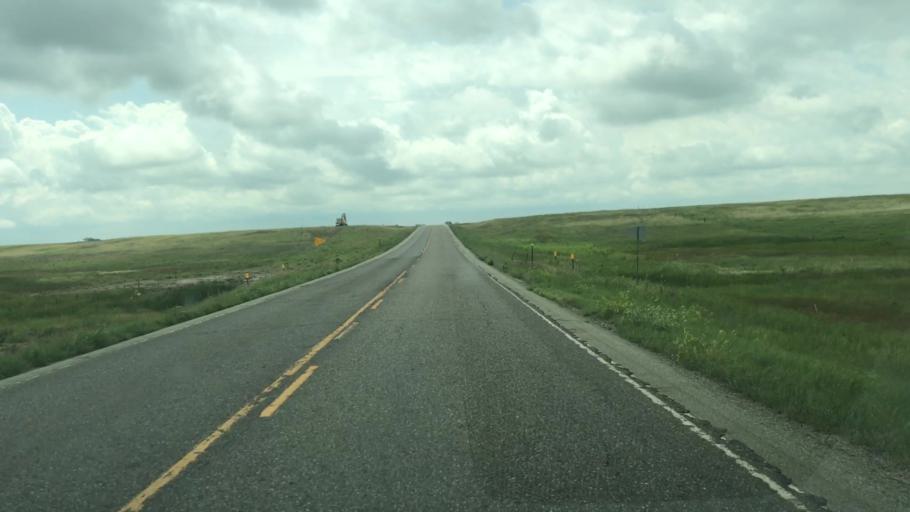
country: US
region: Nebraska
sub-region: Cherry County
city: Valentine
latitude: 43.0664
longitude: -100.5957
